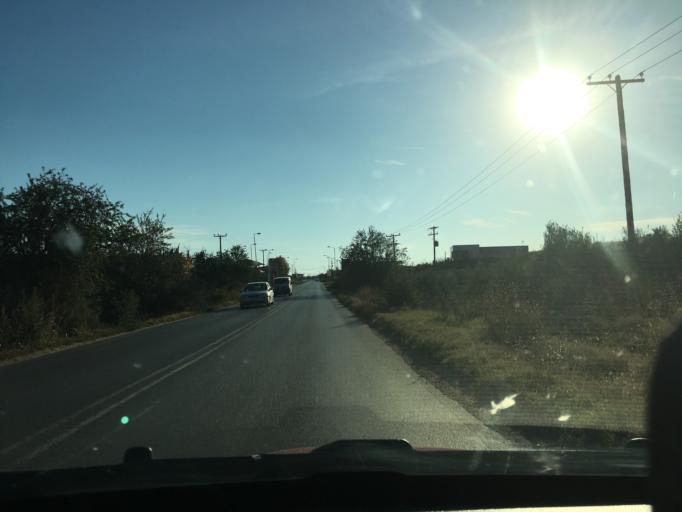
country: GR
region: Central Macedonia
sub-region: Nomos Chalkidikis
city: Olynthos
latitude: 40.2638
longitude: 23.3335
